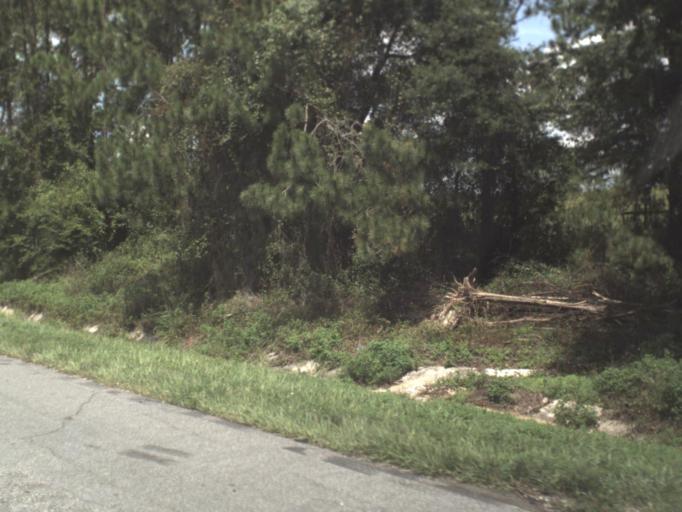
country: US
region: Florida
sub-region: Hernando County
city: Hill 'n Dale
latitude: 28.4718
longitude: -82.2637
